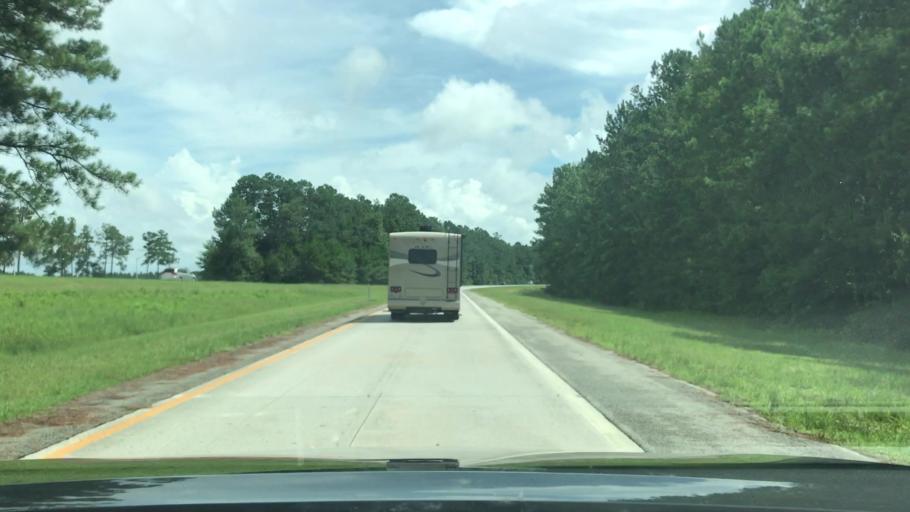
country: US
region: South Carolina
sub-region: Colleton County
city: Walterboro
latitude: 33.0009
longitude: -80.6706
